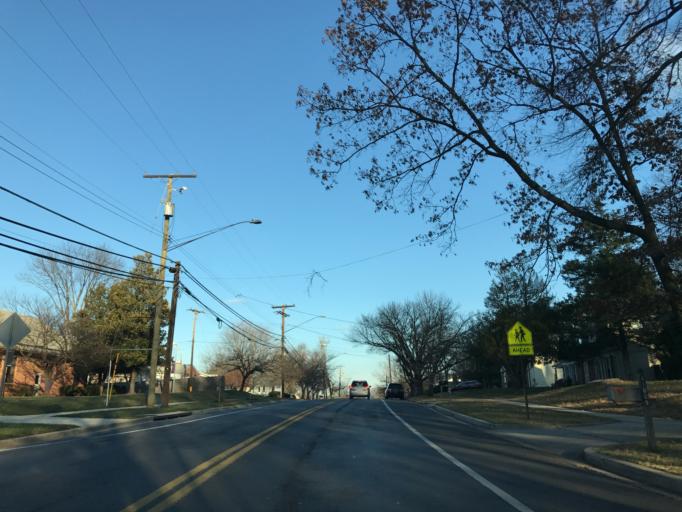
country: US
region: Maryland
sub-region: Montgomery County
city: Kemp Mill
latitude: 39.0467
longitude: -77.0311
